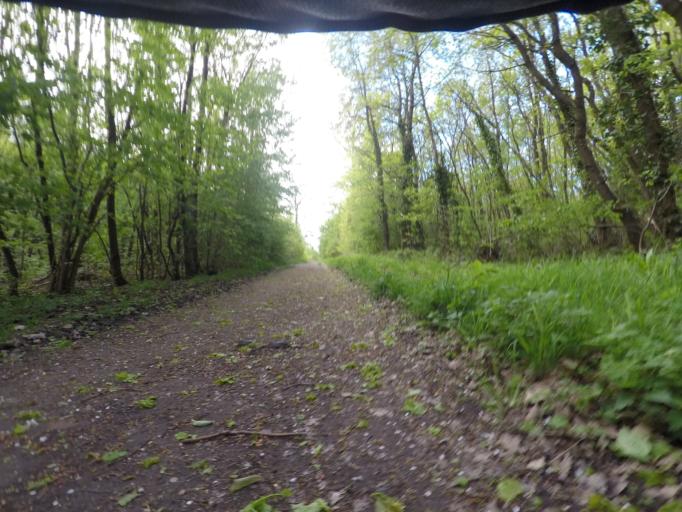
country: AT
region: Lower Austria
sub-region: Politischer Bezirk Modling
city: Perchtoldsdorf
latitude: 48.1728
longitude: 16.2658
